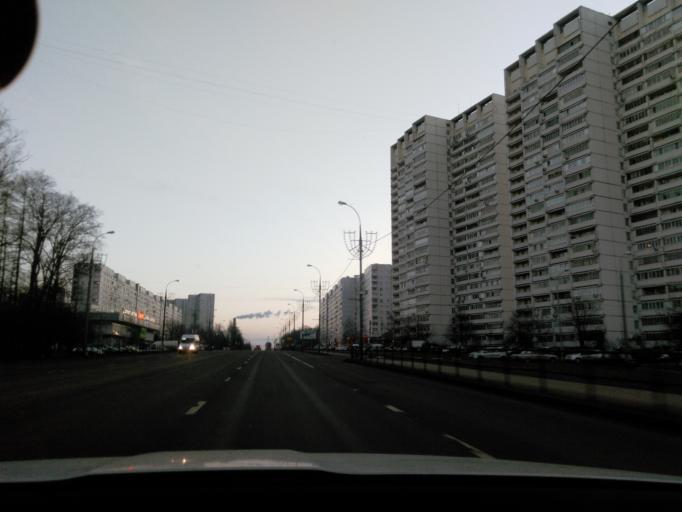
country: RU
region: Moscow
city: Zelenograd
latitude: 55.9928
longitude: 37.1874
